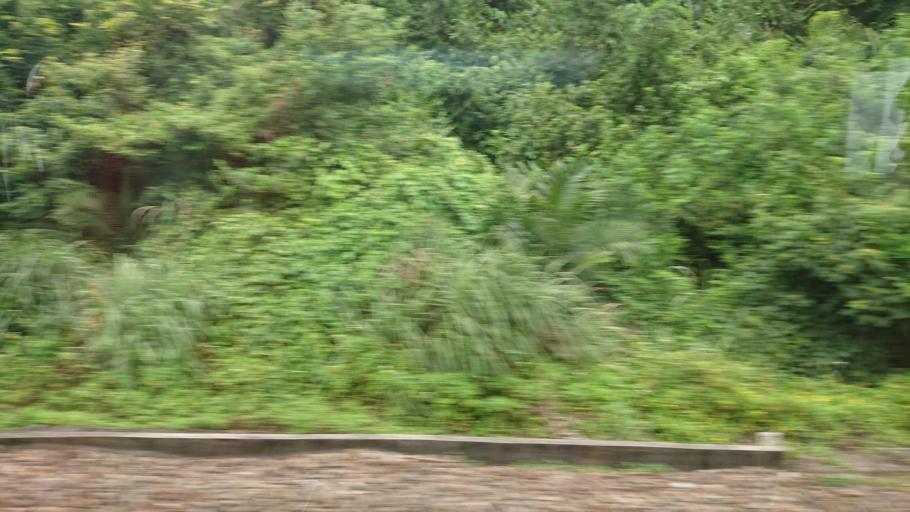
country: TW
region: Taiwan
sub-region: Keelung
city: Keelung
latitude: 24.9602
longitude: 121.9188
